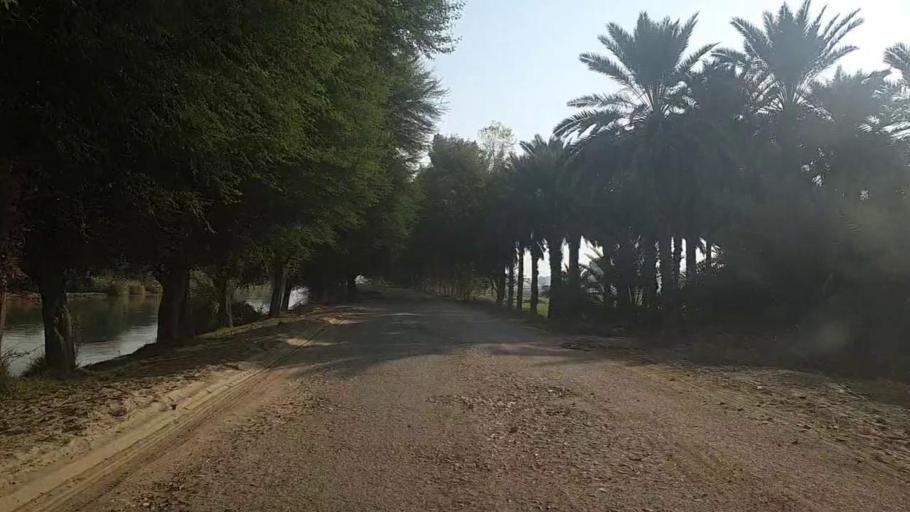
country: PK
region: Sindh
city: Bozdar
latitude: 27.2549
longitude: 68.6766
